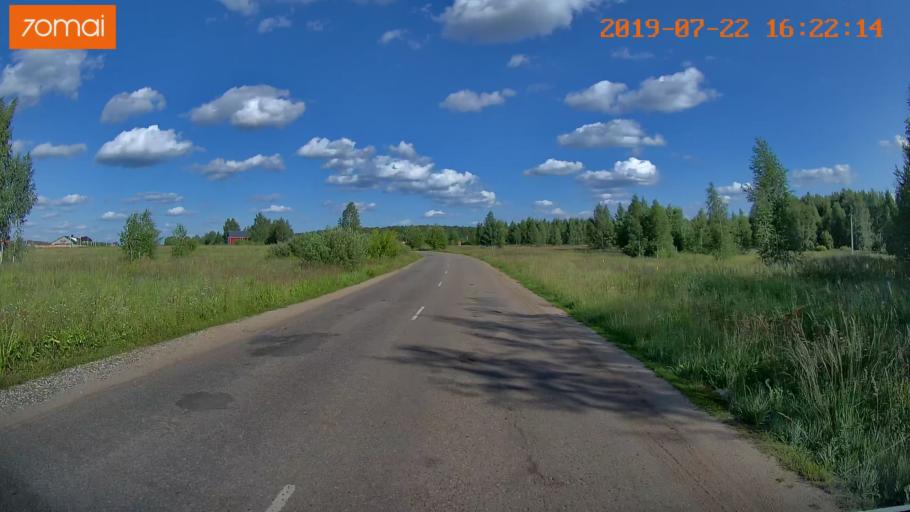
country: RU
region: Ivanovo
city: Novo-Talitsy
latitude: 57.0588
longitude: 40.8800
